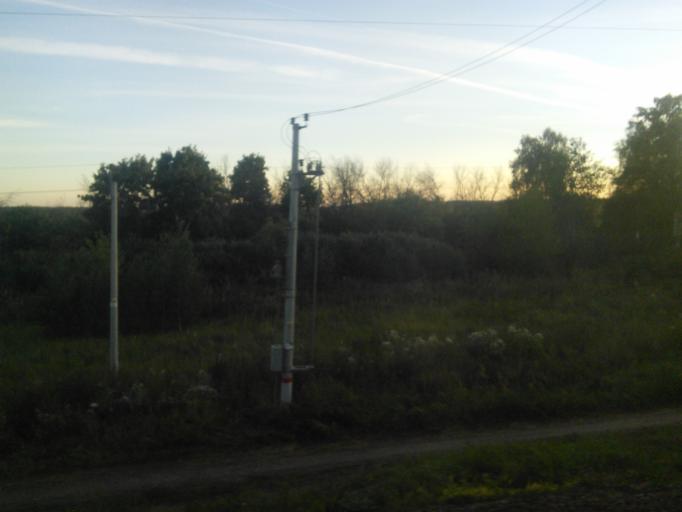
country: RU
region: Moskovskaya
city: Elektrougli
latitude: 55.7377
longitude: 38.1753
